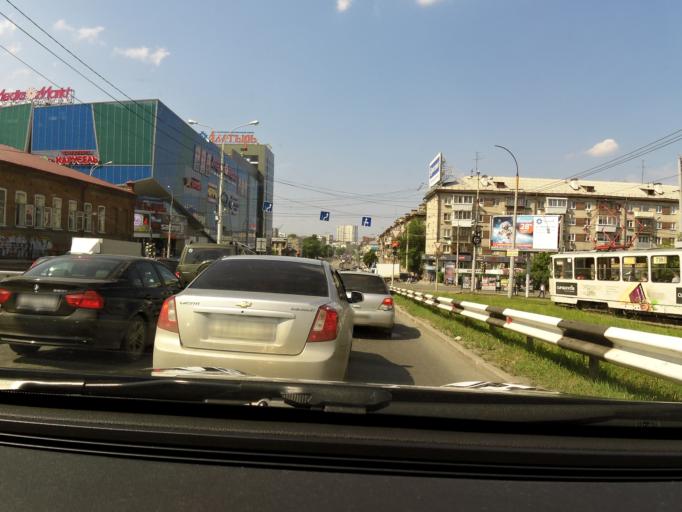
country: RU
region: Sverdlovsk
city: Yekaterinburg
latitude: 56.8316
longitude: 60.5840
